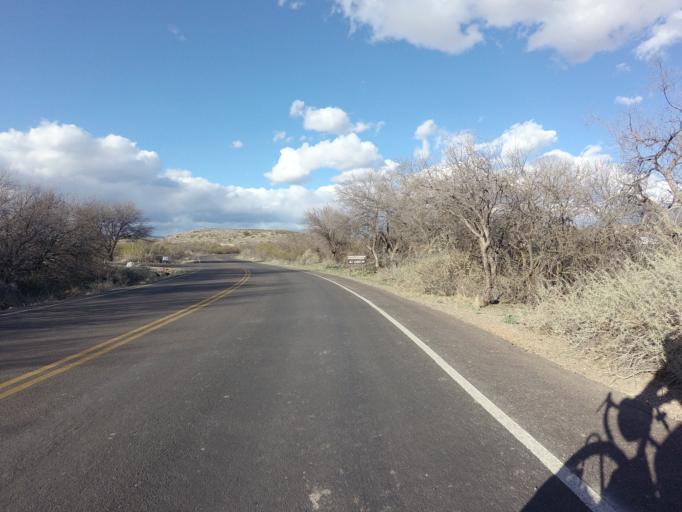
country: US
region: Arizona
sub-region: Yavapai County
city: Cottonwood
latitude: 34.7545
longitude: -112.0184
